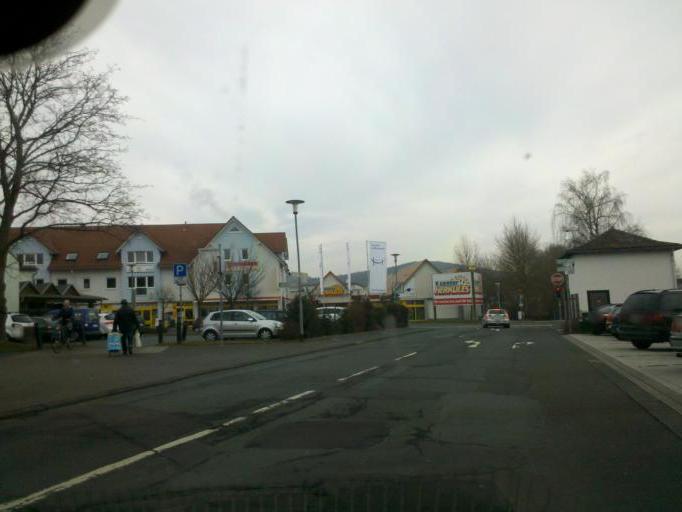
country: DE
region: Hesse
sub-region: Regierungsbezirk Giessen
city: Haiger
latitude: 50.7417
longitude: 8.2057
